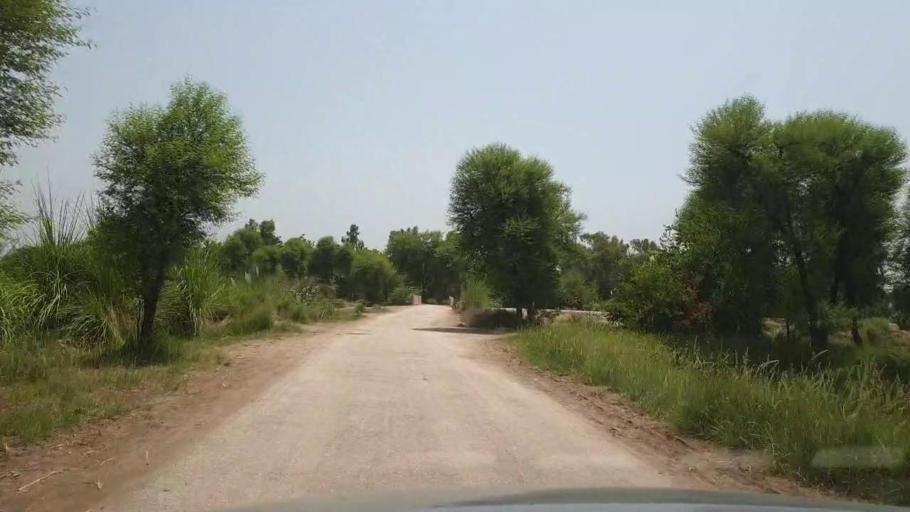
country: PK
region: Sindh
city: Ratodero
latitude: 27.7954
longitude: 68.3470
